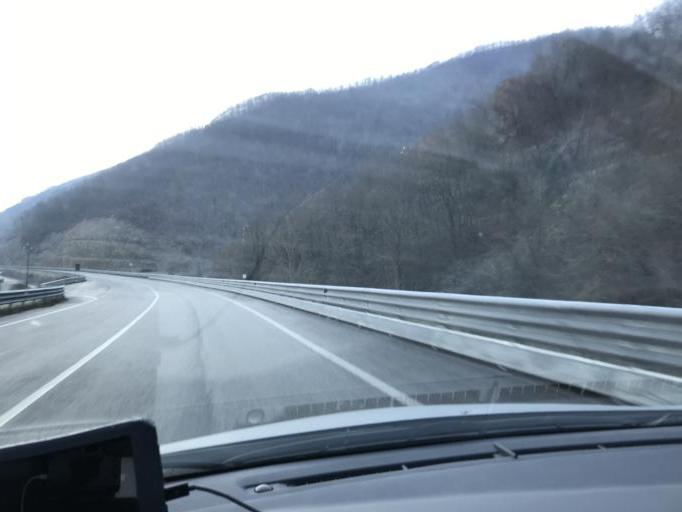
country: IT
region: Latium
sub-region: Provincia di Rieti
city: Cittaducale
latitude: 42.3545
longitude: 12.9390
